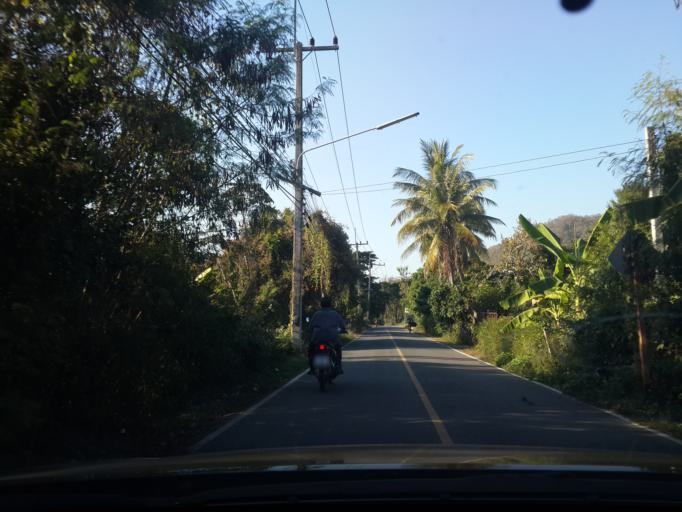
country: TH
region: Chiang Mai
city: San Sai
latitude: 18.9195
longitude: 99.1319
